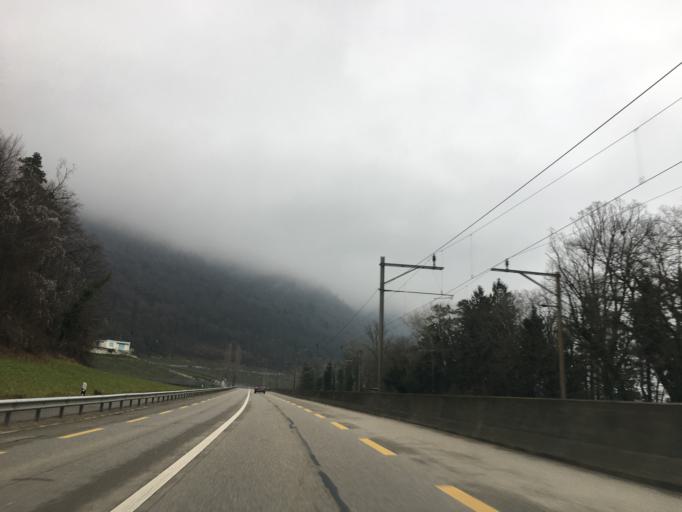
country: CH
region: Bern
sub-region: Jura bernois
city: La Neuveville
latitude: 47.0712
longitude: 7.1121
